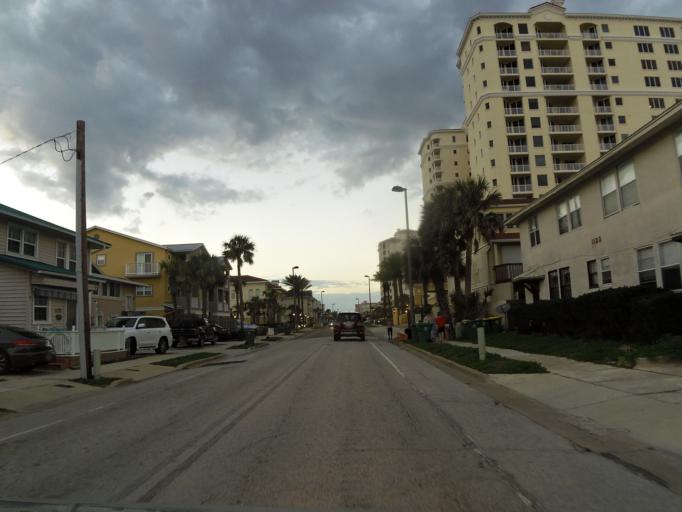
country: US
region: Florida
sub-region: Duval County
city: Jacksonville Beach
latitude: 30.2775
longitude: -81.3873
